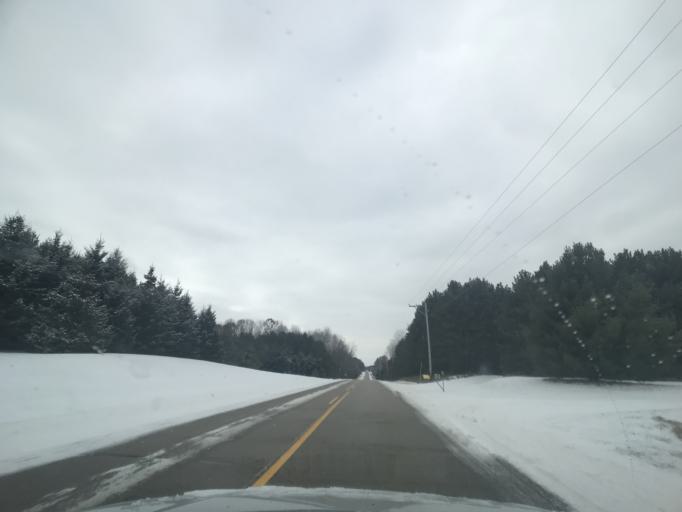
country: US
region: Wisconsin
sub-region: Brown County
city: Suamico
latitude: 44.7063
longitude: -88.0923
